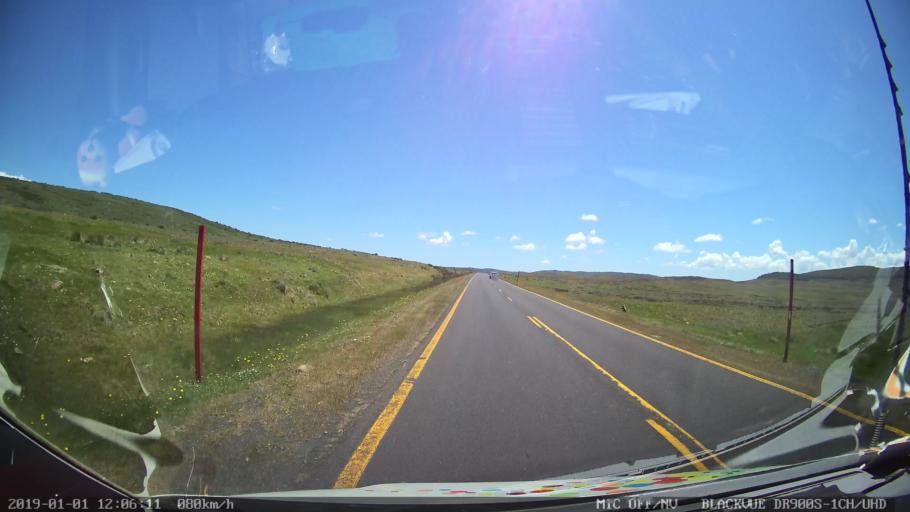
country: AU
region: New South Wales
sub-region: Snowy River
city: Jindabyne
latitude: -35.8481
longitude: 148.4912
